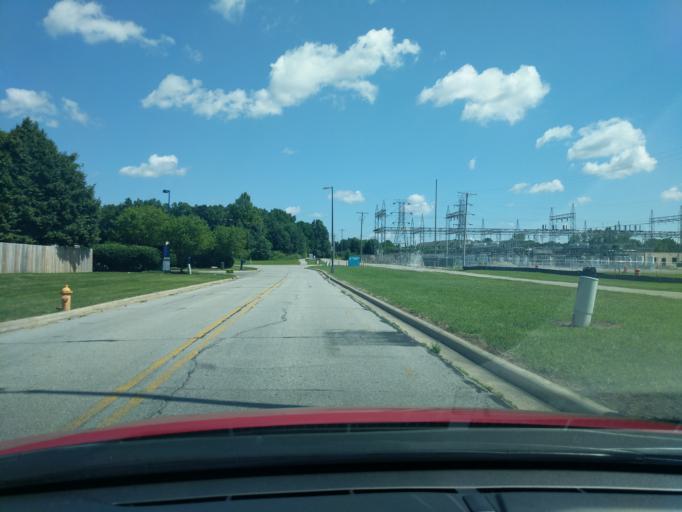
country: US
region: Ohio
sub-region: Franklin County
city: Huber Ridge
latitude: 40.0599
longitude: -82.9083
